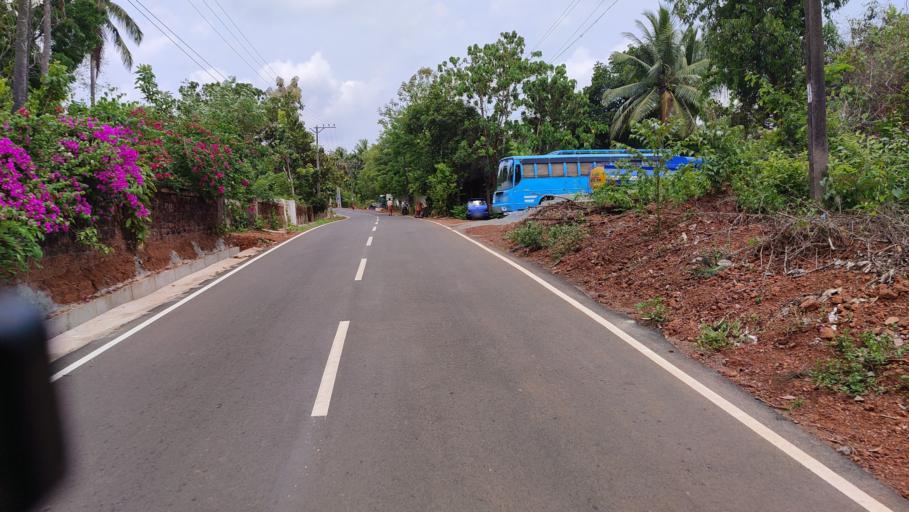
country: IN
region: Kerala
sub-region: Kasaragod District
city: Kannangad
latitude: 12.3192
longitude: 75.1162
